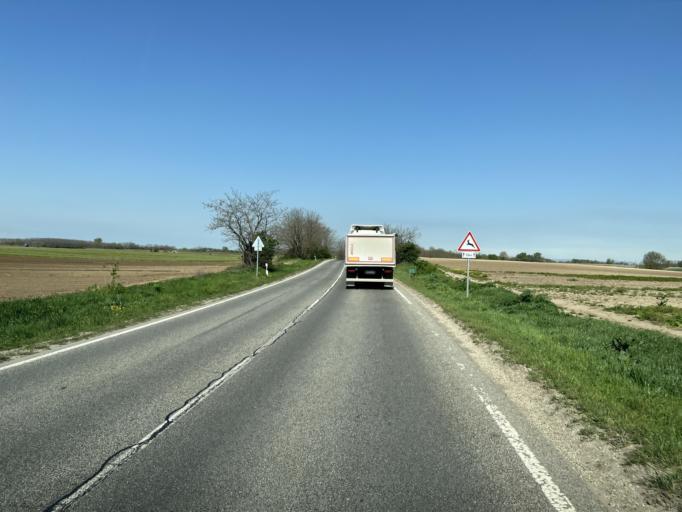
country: HU
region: Pest
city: Alsonemedi
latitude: 47.3227
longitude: 19.1945
